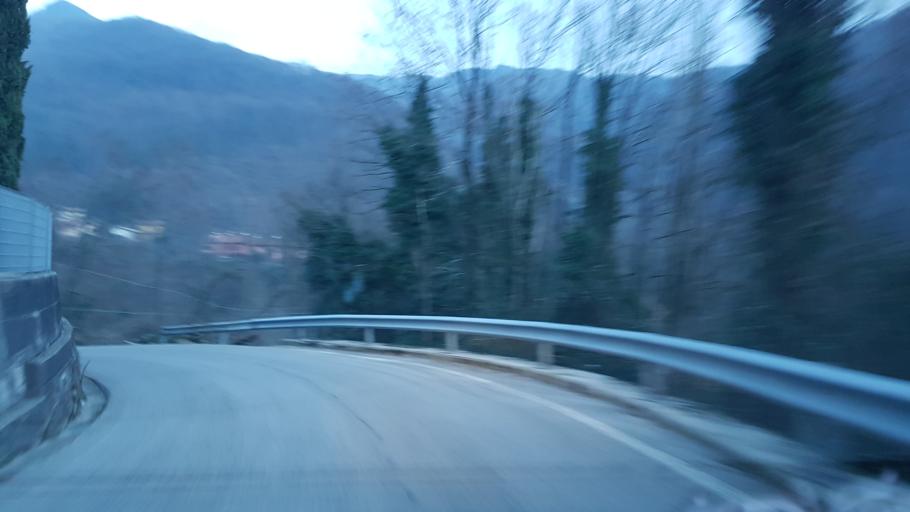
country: IT
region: Friuli Venezia Giulia
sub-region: Provincia di Udine
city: Attimis
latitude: 46.1944
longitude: 13.3364
